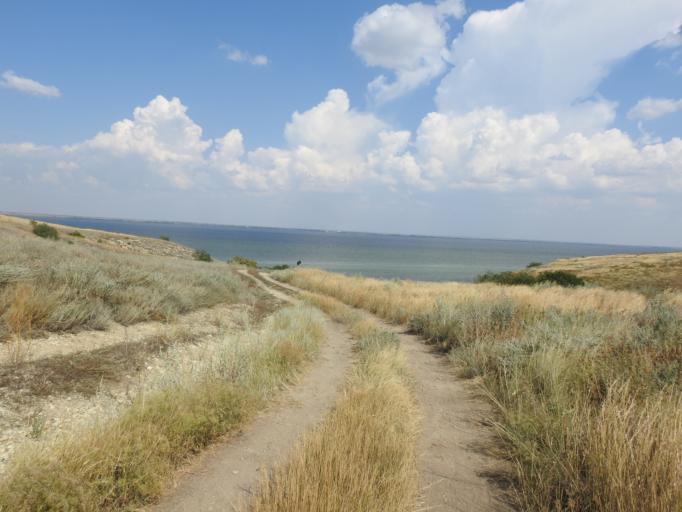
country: RU
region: Saratov
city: Rovnoye
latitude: 50.4921
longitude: 45.7974
